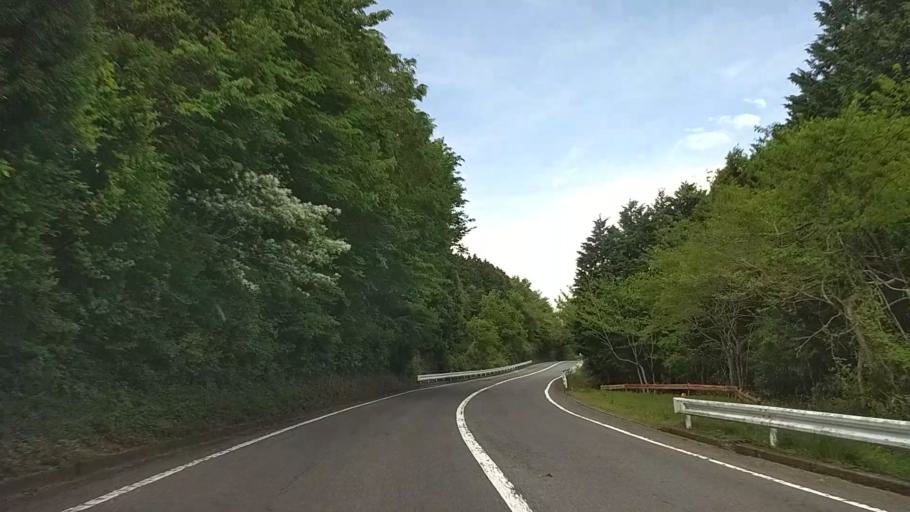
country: JP
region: Kanagawa
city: Yugawara
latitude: 35.2106
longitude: 139.0956
